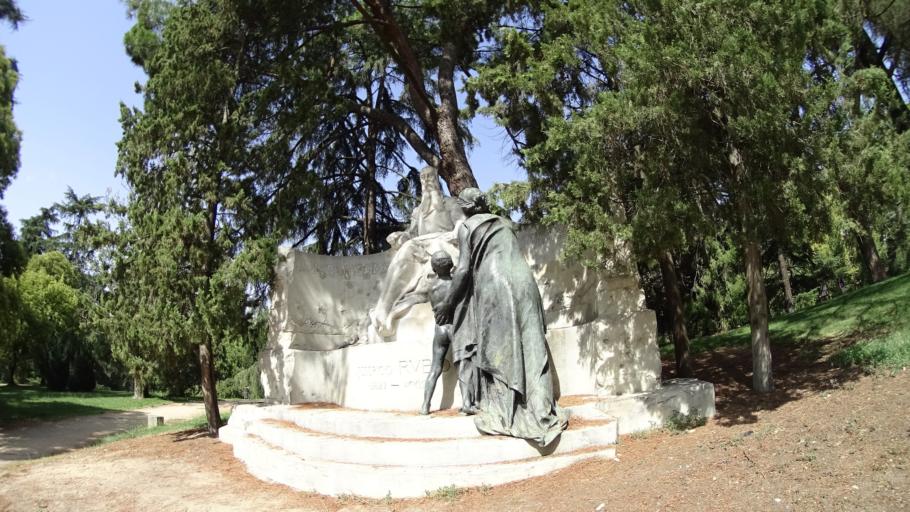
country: ES
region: Madrid
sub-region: Provincia de Madrid
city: Moncloa-Aravaca
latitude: 40.4357
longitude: -3.7243
